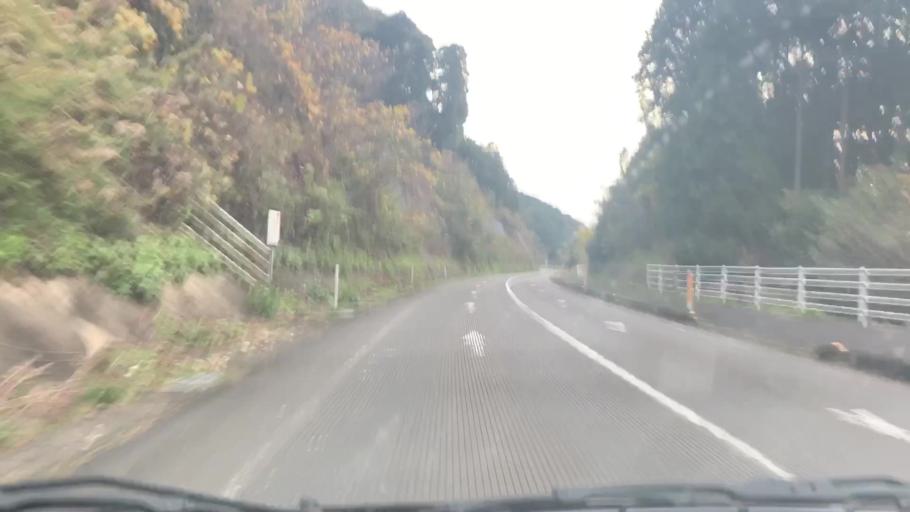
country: JP
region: Saga Prefecture
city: Kashima
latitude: 33.0464
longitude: 130.0717
